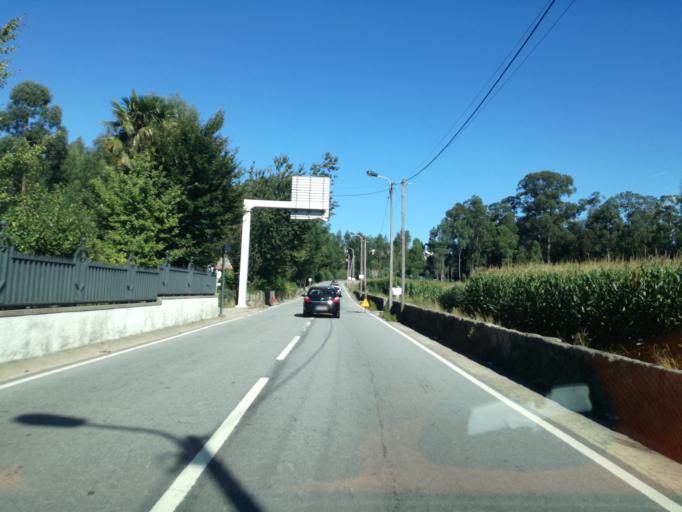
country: PT
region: Porto
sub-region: Maia
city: Anta
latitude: 41.2864
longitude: -8.6010
